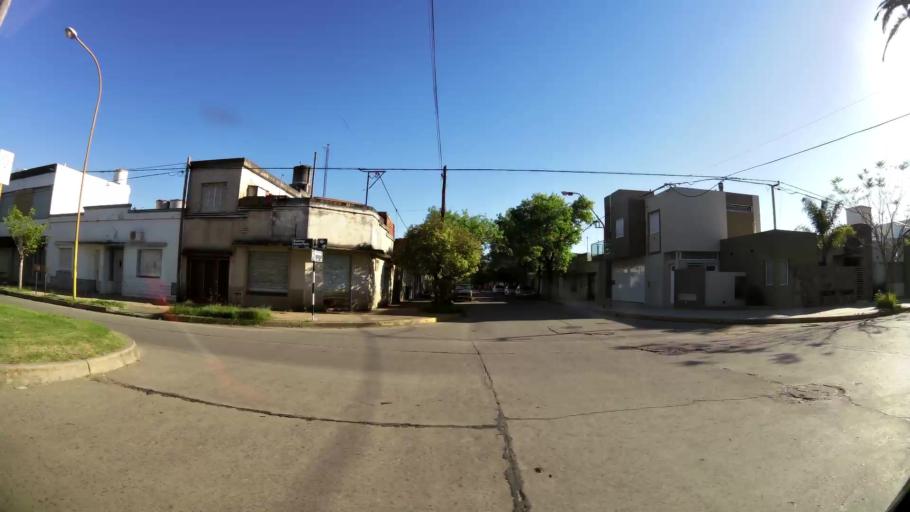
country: AR
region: Cordoba
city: San Francisco
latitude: -31.4362
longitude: -62.0822
